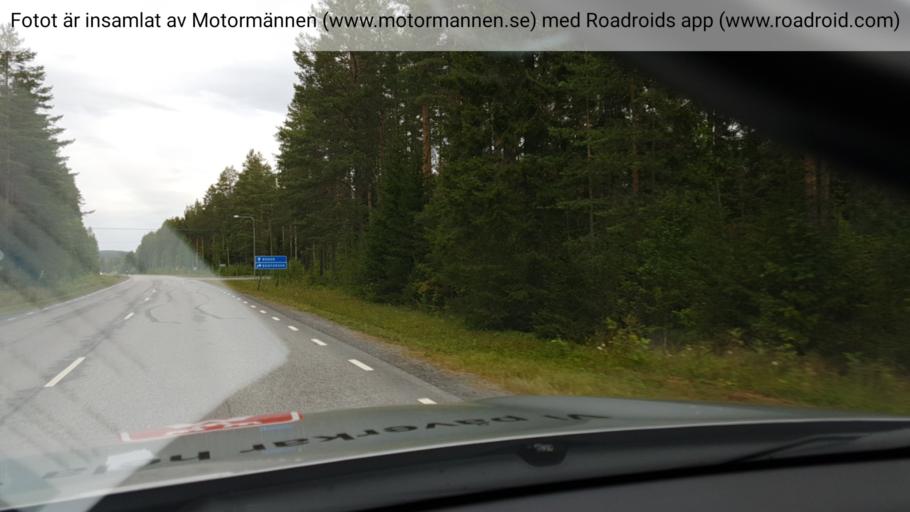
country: SE
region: Norrbotten
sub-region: Bodens Kommun
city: Boden
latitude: 65.8068
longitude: 21.6558
